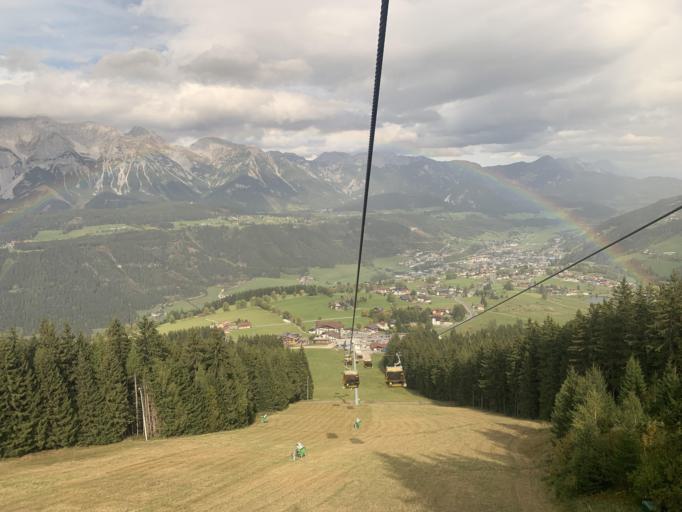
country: AT
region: Styria
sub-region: Politischer Bezirk Liezen
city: Schladming
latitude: 47.3716
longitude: 13.6497
